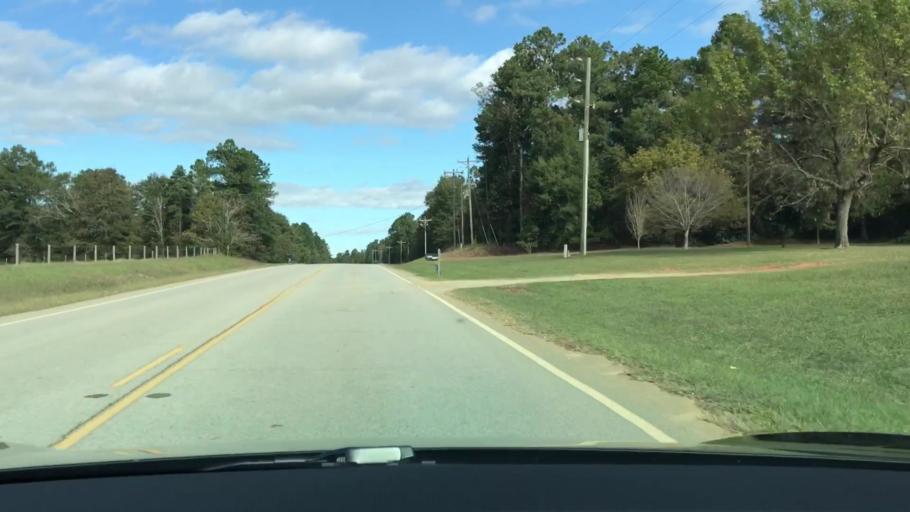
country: US
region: Georgia
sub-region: Jefferson County
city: Louisville
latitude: 33.0831
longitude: -82.4134
